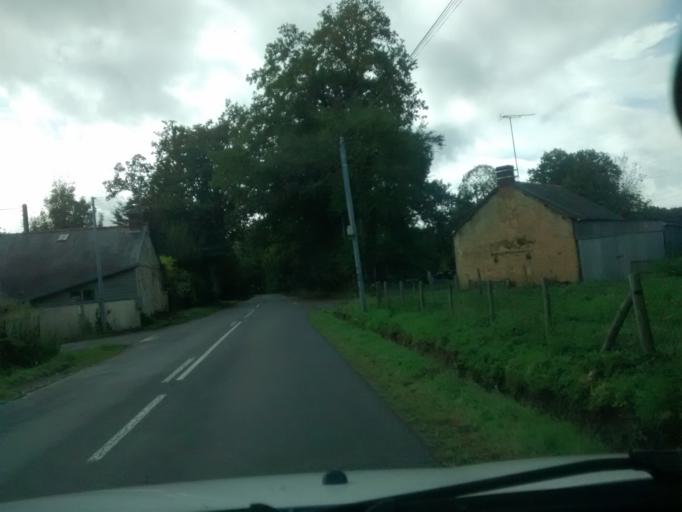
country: FR
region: Brittany
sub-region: Departement d'Ille-et-Vilaine
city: Chateaubourg
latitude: 48.1357
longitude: -1.4061
